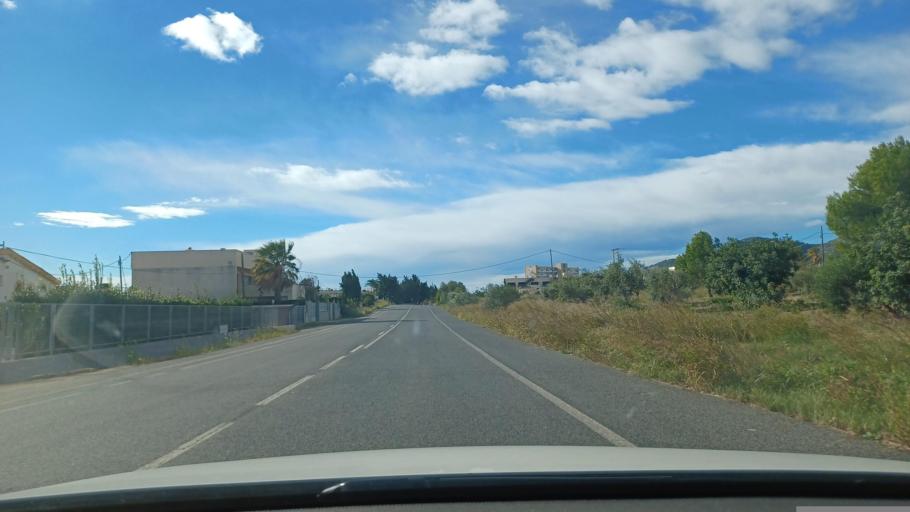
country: ES
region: Catalonia
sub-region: Provincia de Tarragona
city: Sant Carles de la Rapita
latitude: 40.5922
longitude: 0.5668
